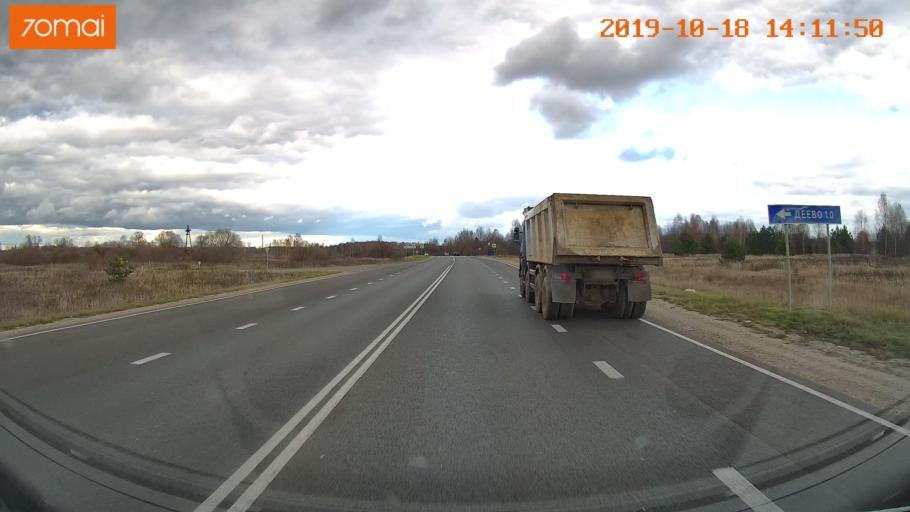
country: RU
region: Rjazan
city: Spas-Klepiki
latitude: 55.1402
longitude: 40.2359
